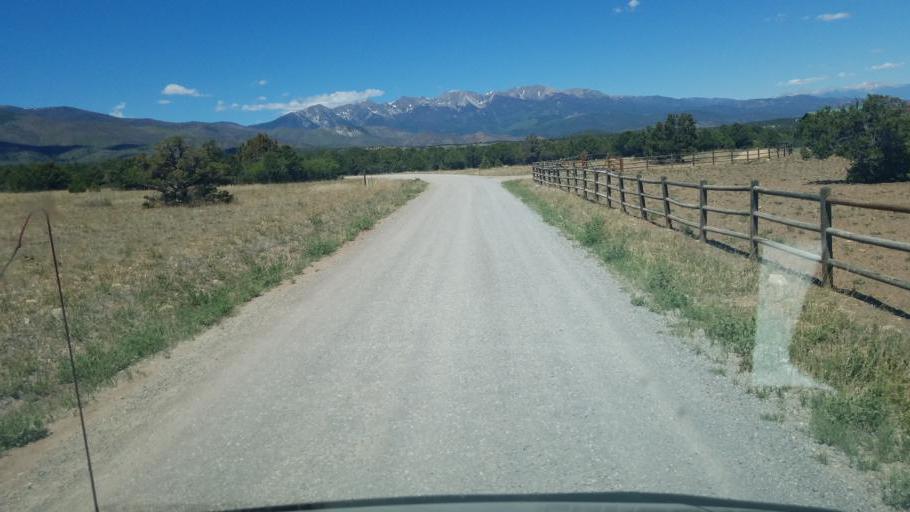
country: US
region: Colorado
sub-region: Custer County
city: Westcliffe
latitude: 38.3119
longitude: -105.6724
